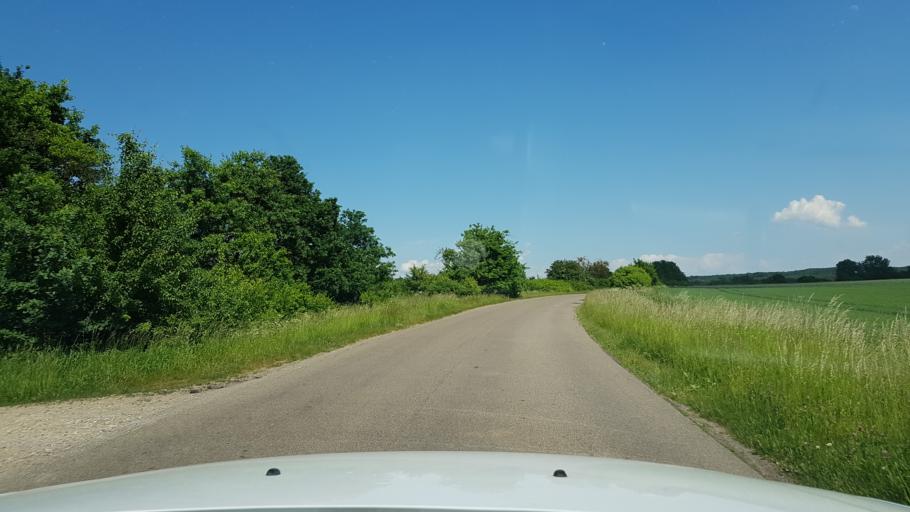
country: PL
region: West Pomeranian Voivodeship
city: Trzcinsko Zdroj
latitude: 53.0345
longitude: 14.6107
